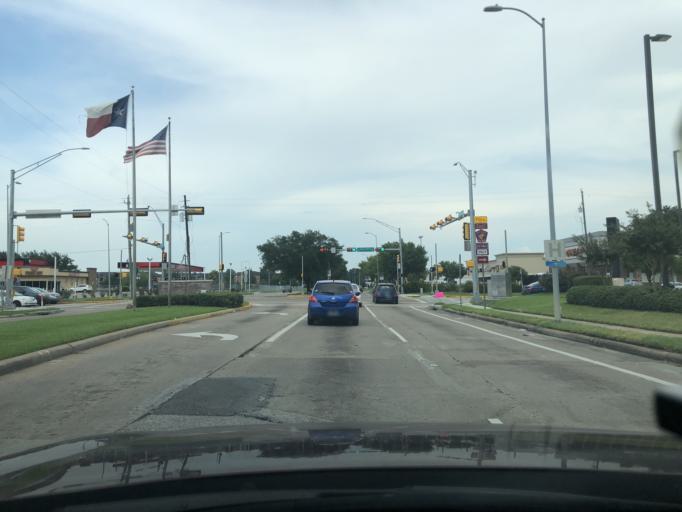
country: US
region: Texas
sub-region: Fort Bend County
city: Mission Bend
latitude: 29.7297
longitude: -95.6064
